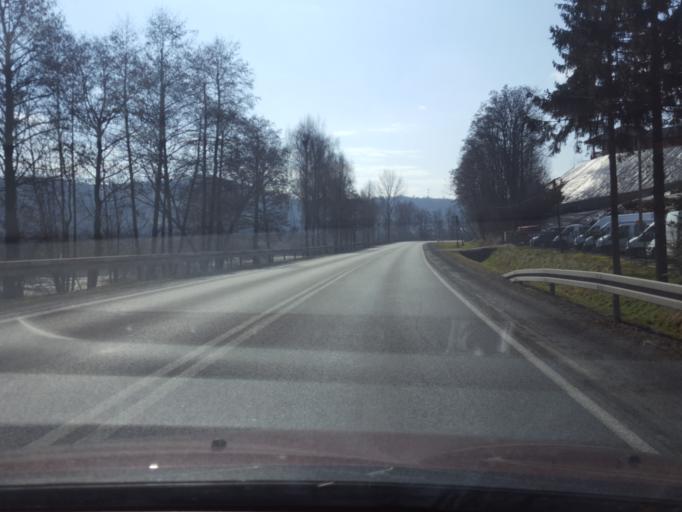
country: PL
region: Lesser Poland Voivodeship
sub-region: Powiat nowosadecki
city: Lososina Dolna
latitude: 49.6989
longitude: 20.6597
